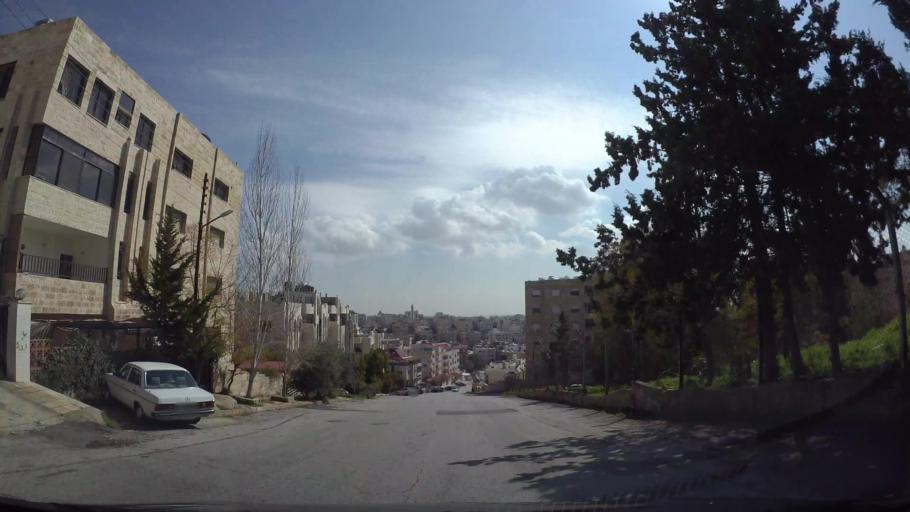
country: JO
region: Amman
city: Al Jubayhah
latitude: 31.9922
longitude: 35.8997
